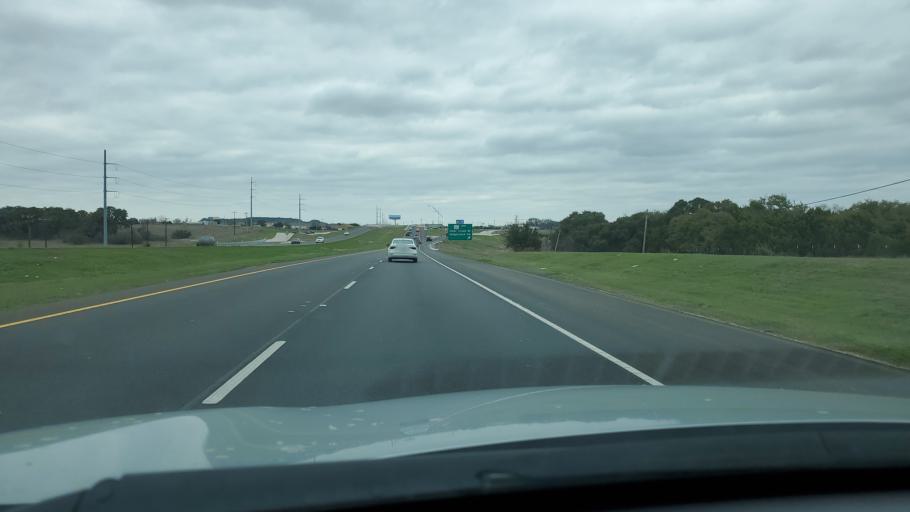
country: US
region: Texas
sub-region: Bell County
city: Killeen
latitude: 31.0521
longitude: -97.7635
